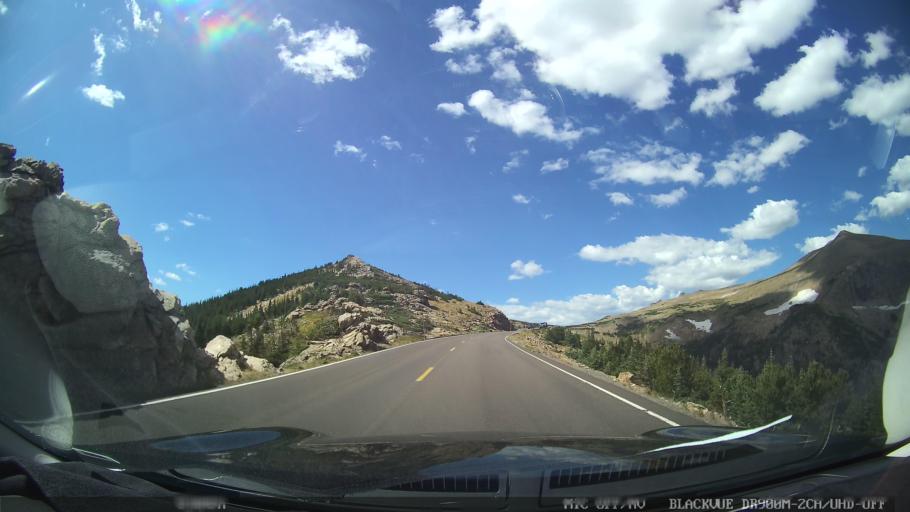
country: US
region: Colorado
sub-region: Larimer County
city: Estes Park
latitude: 40.3984
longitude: -105.6737
